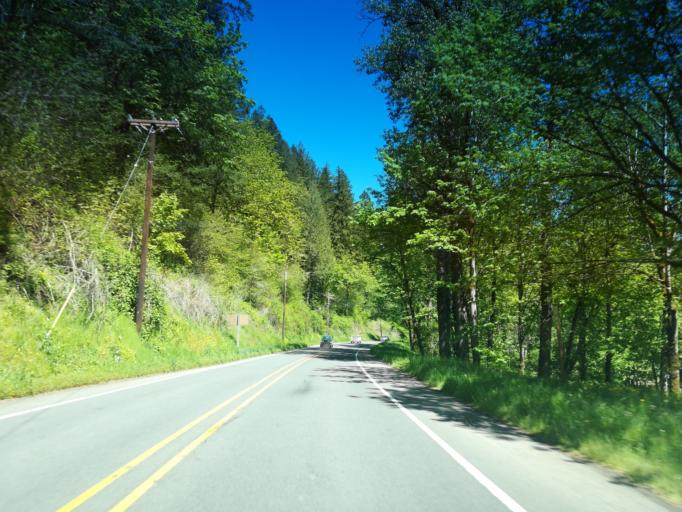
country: US
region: Oregon
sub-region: Multnomah County
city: Troutdale
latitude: 45.5174
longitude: -122.3577
